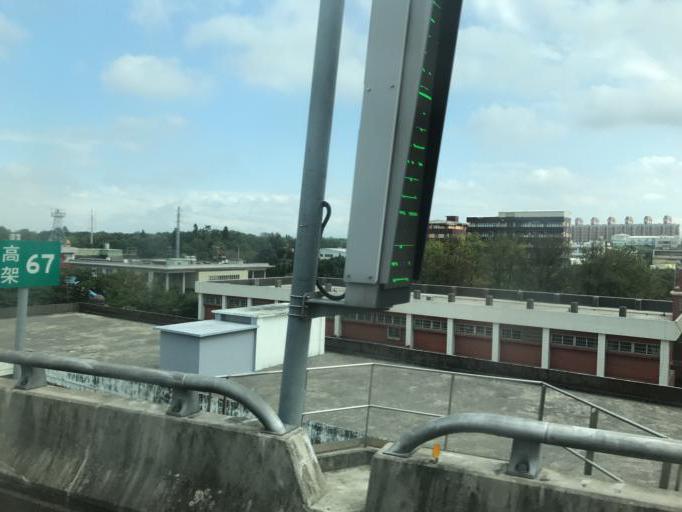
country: TW
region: Taiwan
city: Daxi
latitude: 24.9264
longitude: 121.1730
